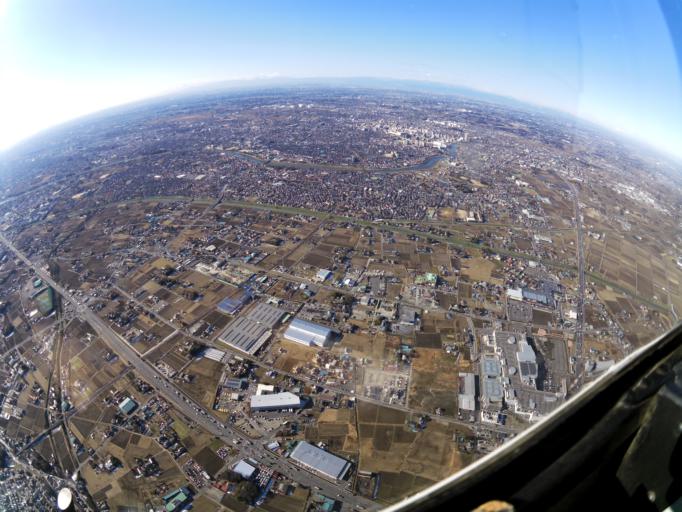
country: JP
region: Saitama
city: Kasukabe
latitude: 35.9858
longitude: 139.7954
